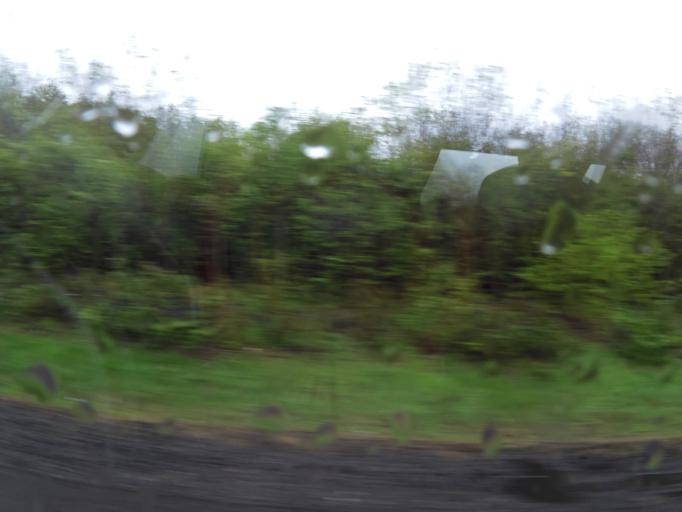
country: IE
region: Leinster
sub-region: Kildare
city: Leixlip
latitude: 53.3584
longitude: -6.5198
